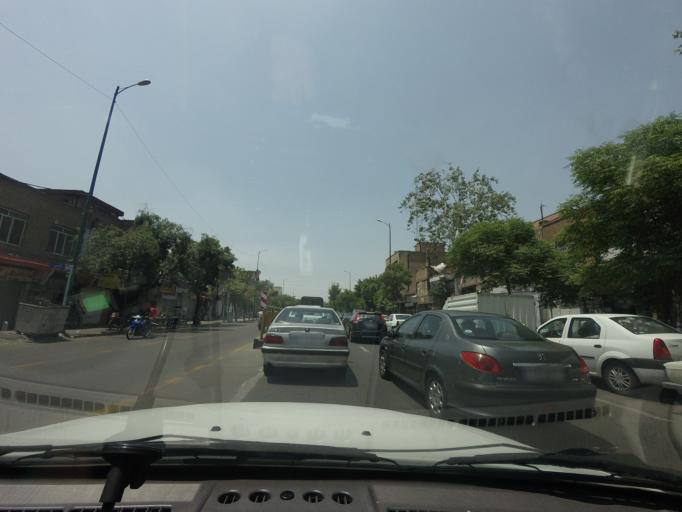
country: IR
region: Tehran
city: Tehran
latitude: 35.6696
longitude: 51.4325
